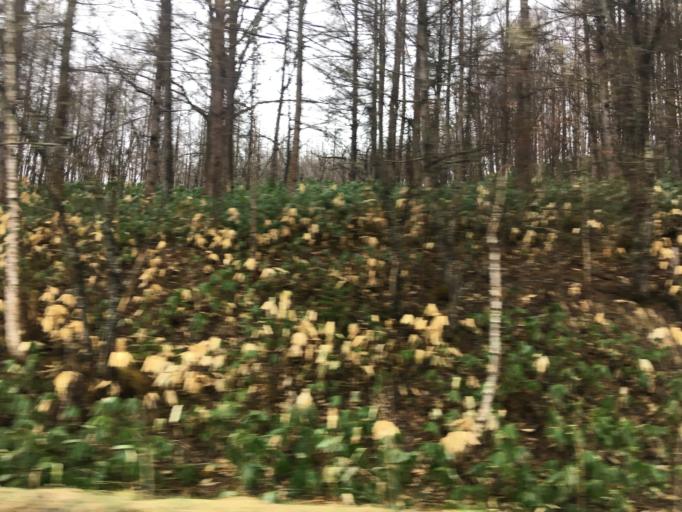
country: JP
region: Hokkaido
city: Nayoro
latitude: 44.0735
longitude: 142.4152
